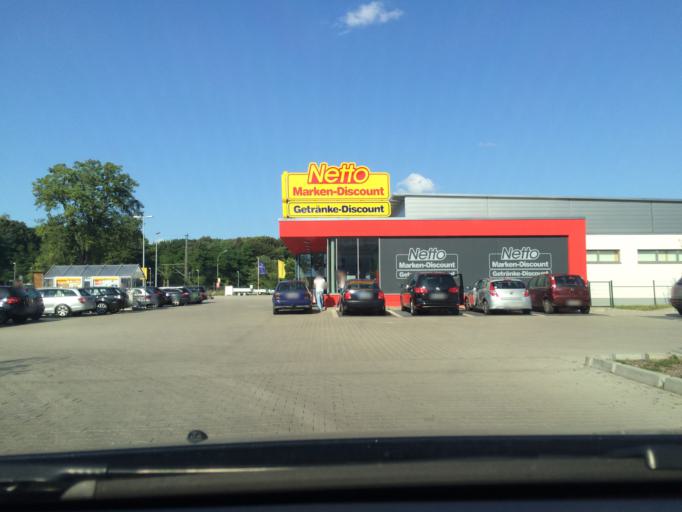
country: DE
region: Mecklenburg-Vorpommern
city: Niepars
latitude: 54.2998
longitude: 12.9298
